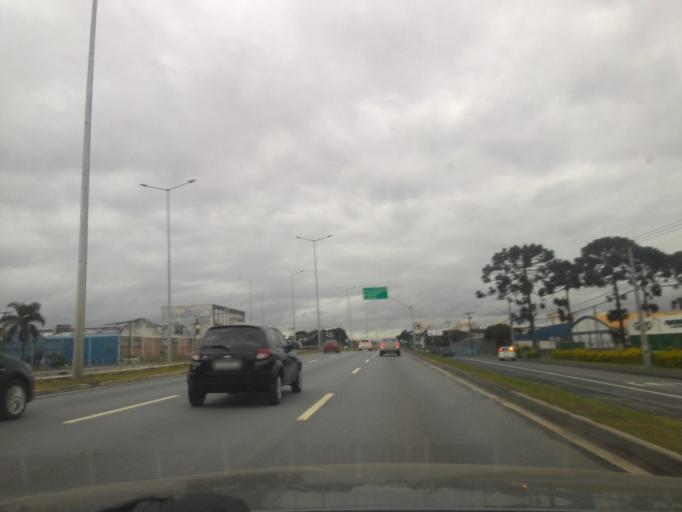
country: BR
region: Parana
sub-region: Sao Jose Dos Pinhais
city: Sao Jose dos Pinhais
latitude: -25.5206
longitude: -49.2938
